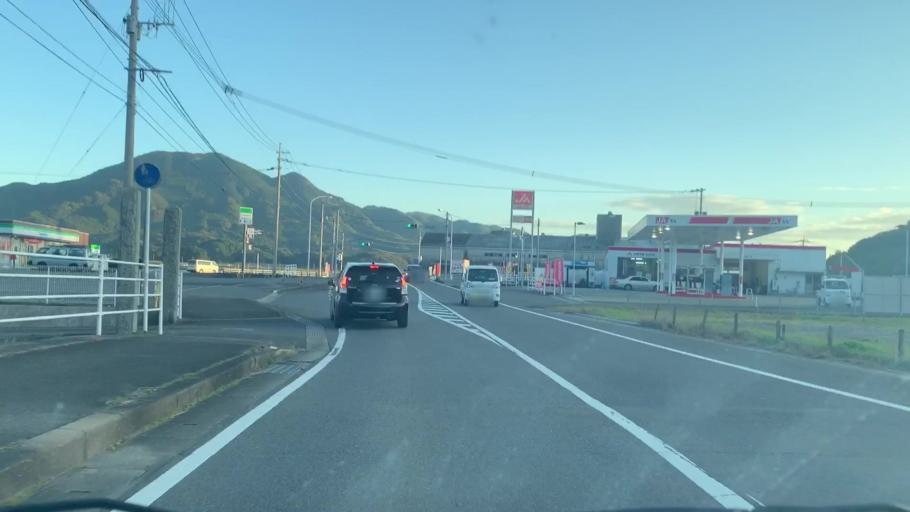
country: JP
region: Saga Prefecture
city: Imaricho-ko
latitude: 33.3023
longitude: 129.9686
